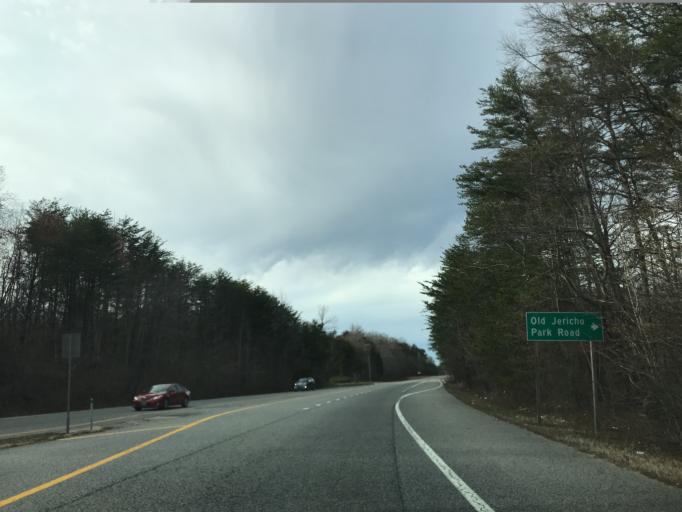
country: US
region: Maryland
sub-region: Prince George's County
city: Glenn Dale
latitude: 39.0197
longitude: -76.7685
